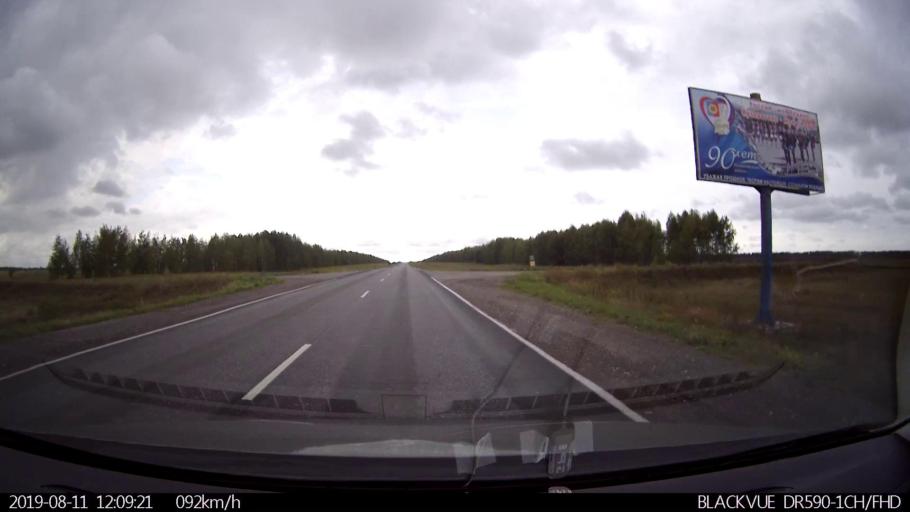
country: RU
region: Ulyanovsk
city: Silikatnyy
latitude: 53.9937
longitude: 48.0486
